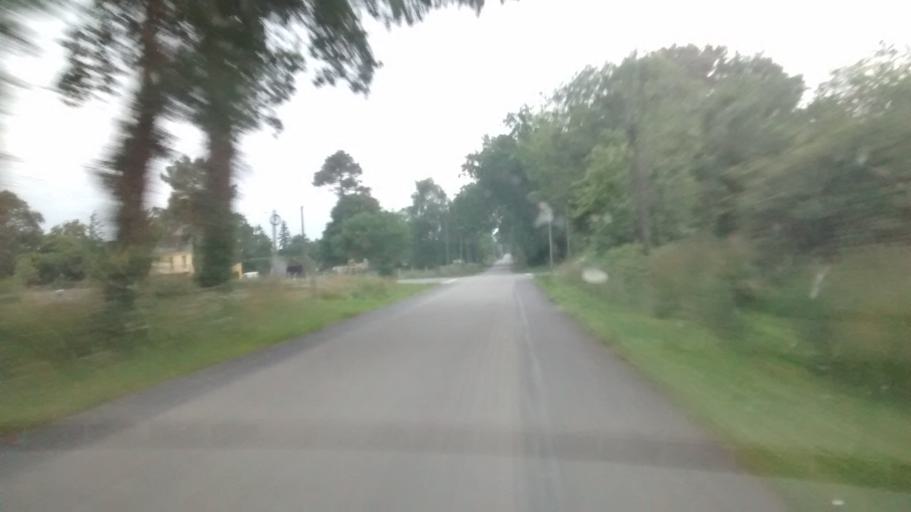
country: FR
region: Brittany
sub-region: Departement du Morbihan
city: Pluherlin
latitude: 47.7337
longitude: -2.3271
